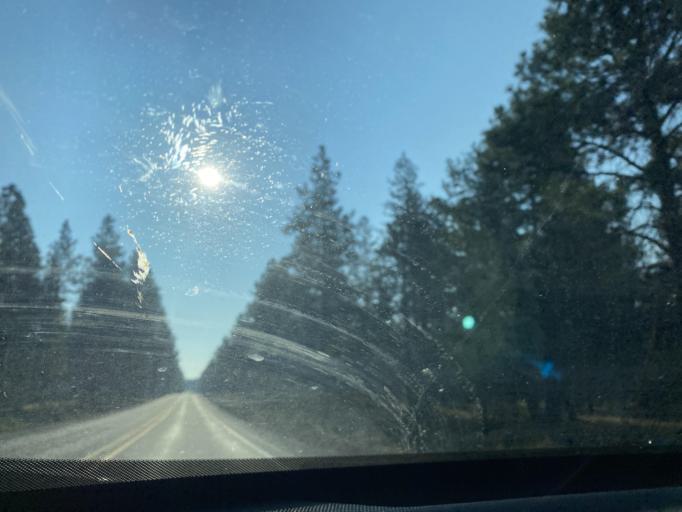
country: US
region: Oregon
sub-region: Deschutes County
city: Sunriver
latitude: 43.8694
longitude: -121.4282
